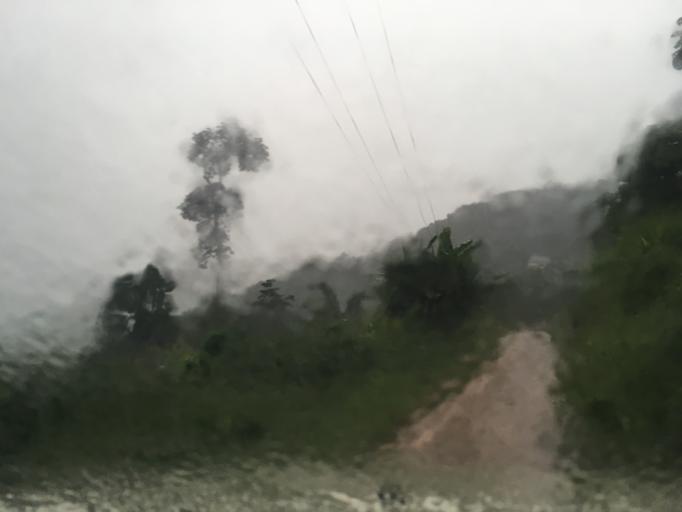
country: LA
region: Oudomxai
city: Muang La
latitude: 21.2383
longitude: 101.9556
